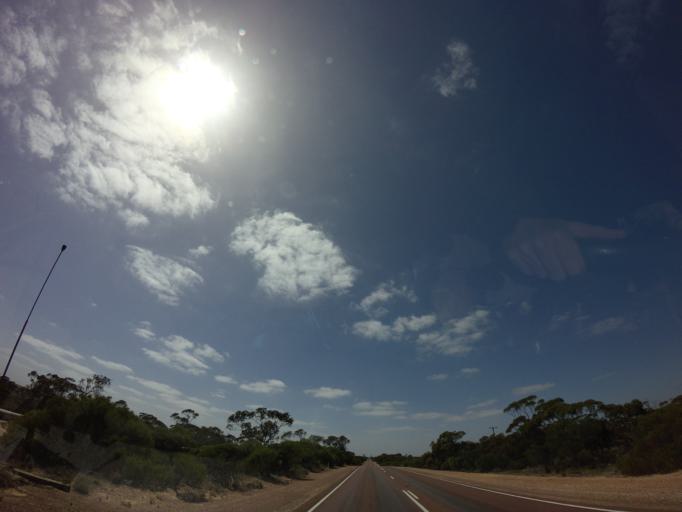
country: AU
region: South Australia
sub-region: Kimba
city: Caralue
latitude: -33.1163
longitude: 135.5366
